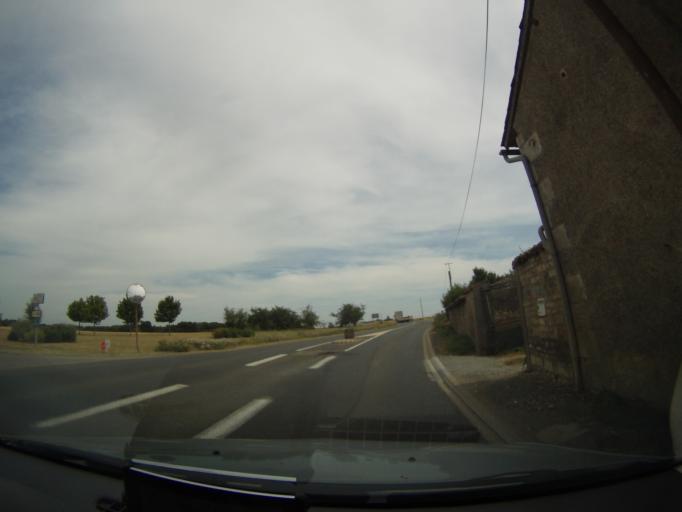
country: FR
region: Poitou-Charentes
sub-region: Departement de la Vienne
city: Mirebeau
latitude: 46.7450
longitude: 0.1778
